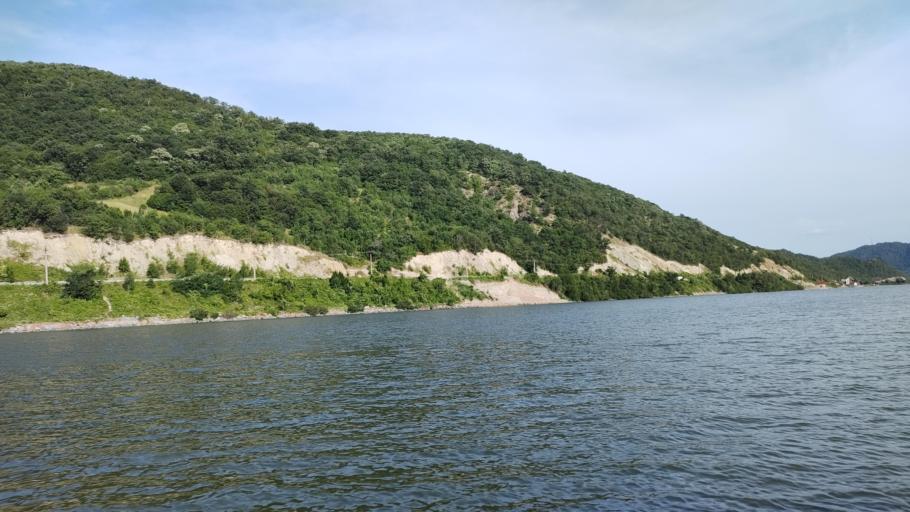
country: RO
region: Mehedinti
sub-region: Comuna Svinita
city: Svinita
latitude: 44.5689
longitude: 22.0290
